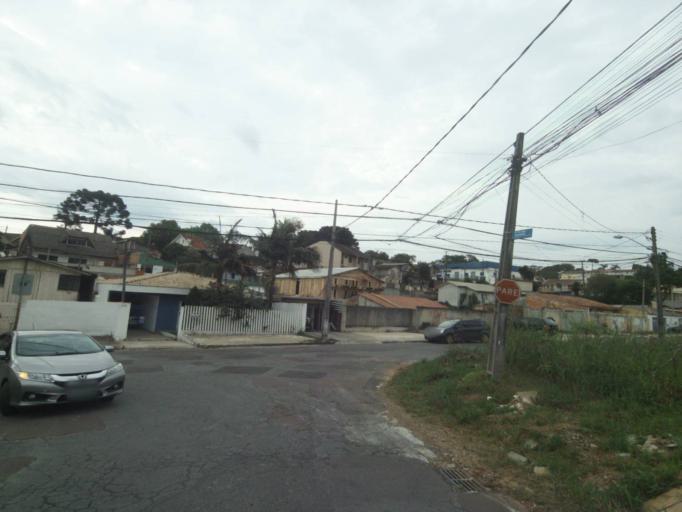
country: BR
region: Parana
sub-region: Curitiba
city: Curitiba
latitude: -25.3976
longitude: -49.2924
